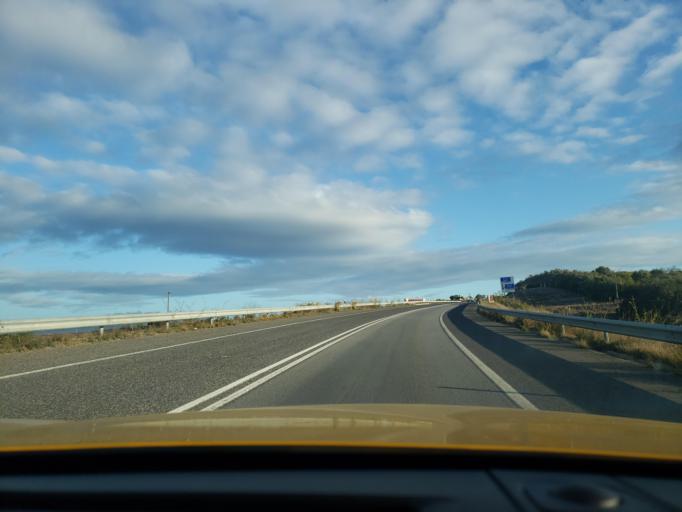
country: PT
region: Faro
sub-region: Portimao
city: Portimao
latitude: 37.1673
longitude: -8.5697
